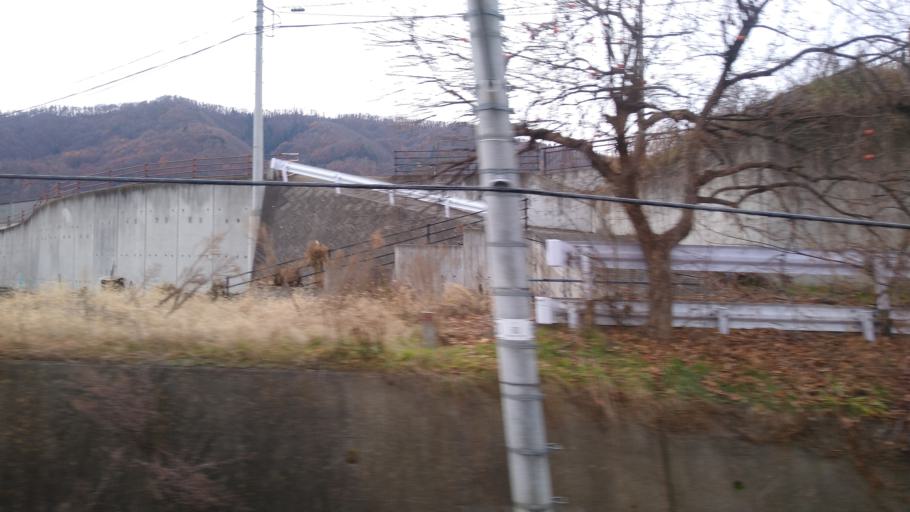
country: JP
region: Nagano
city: Ueda
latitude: 36.3834
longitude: 138.2646
